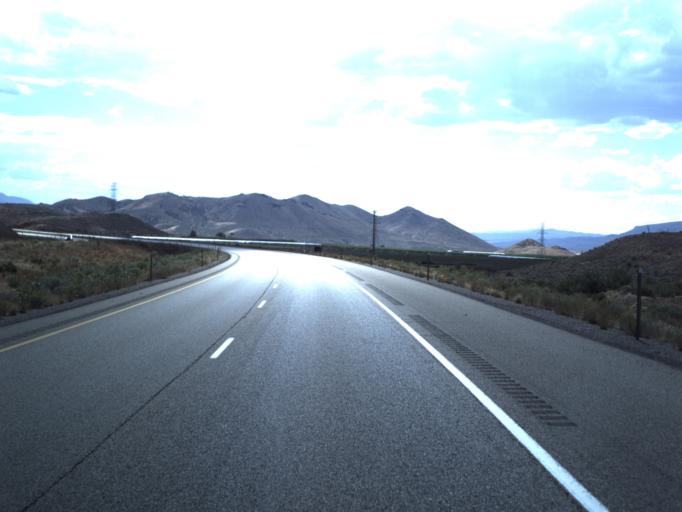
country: US
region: Utah
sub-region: Sevier County
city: Aurora
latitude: 38.9051
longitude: -111.9014
